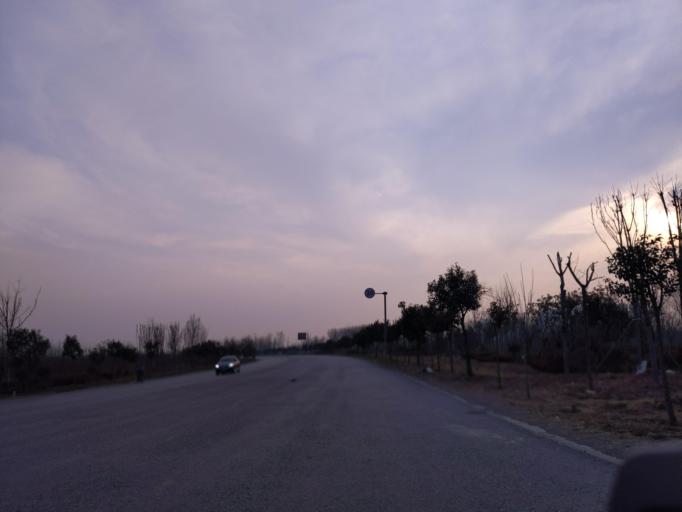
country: CN
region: Henan Sheng
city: Puyang
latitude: 35.8168
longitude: 114.9693
